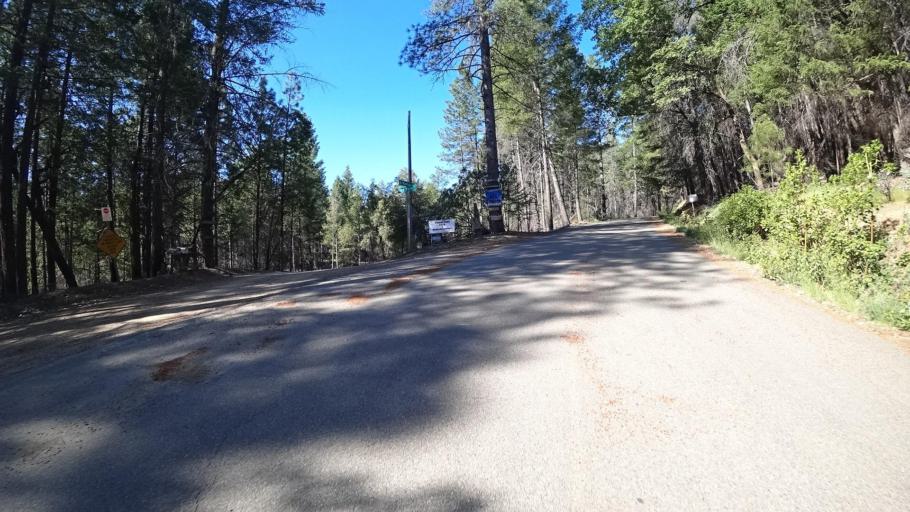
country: US
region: California
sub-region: Lake County
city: Upper Lake
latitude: 39.4001
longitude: -122.9577
